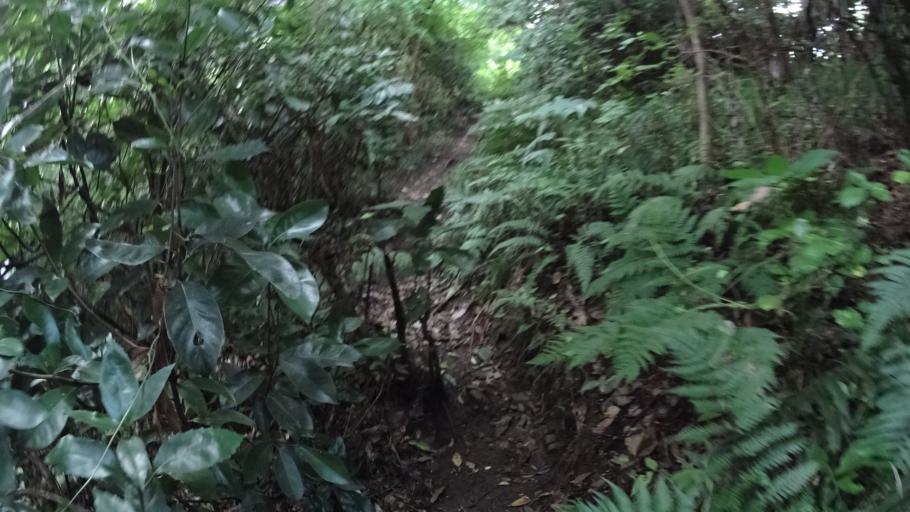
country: JP
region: Kanagawa
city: Yokosuka
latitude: 35.2812
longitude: 139.6245
